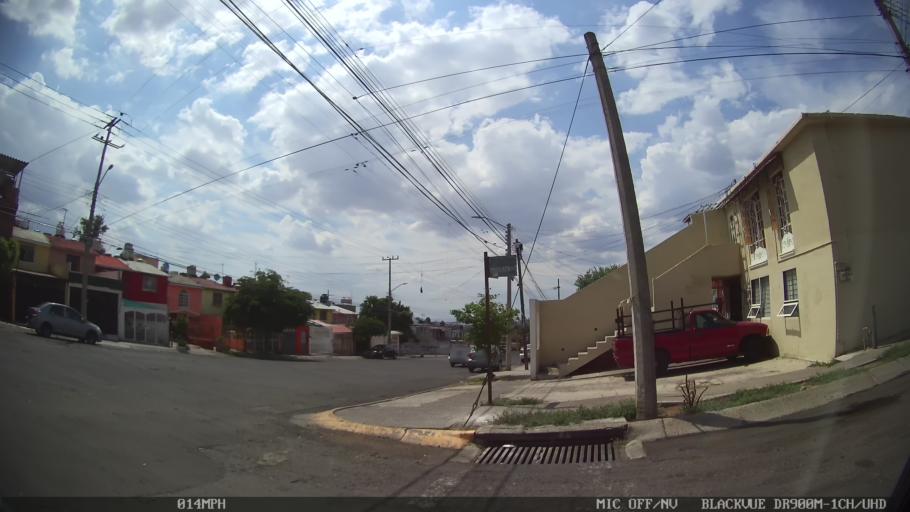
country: MX
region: Jalisco
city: Tonala
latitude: 20.6229
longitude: -103.2611
